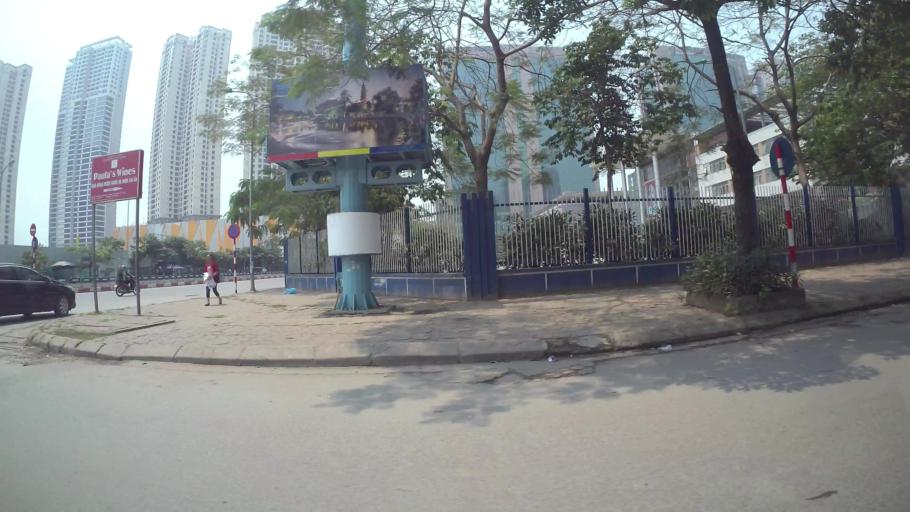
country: VN
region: Ha Noi
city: Thanh Xuan
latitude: 21.0052
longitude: 105.7980
